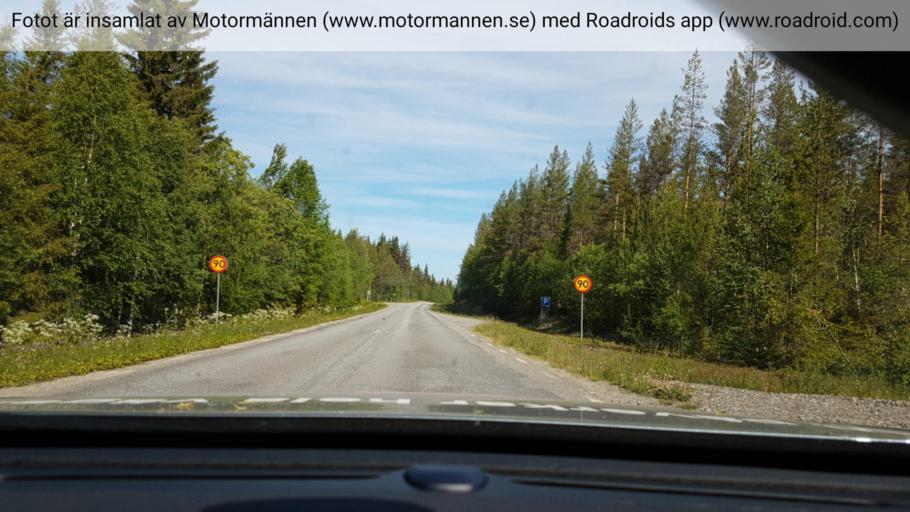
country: SE
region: Vaesterbotten
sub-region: Vilhelmina Kommun
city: Sjoberg
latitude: 64.5873
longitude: 15.8705
